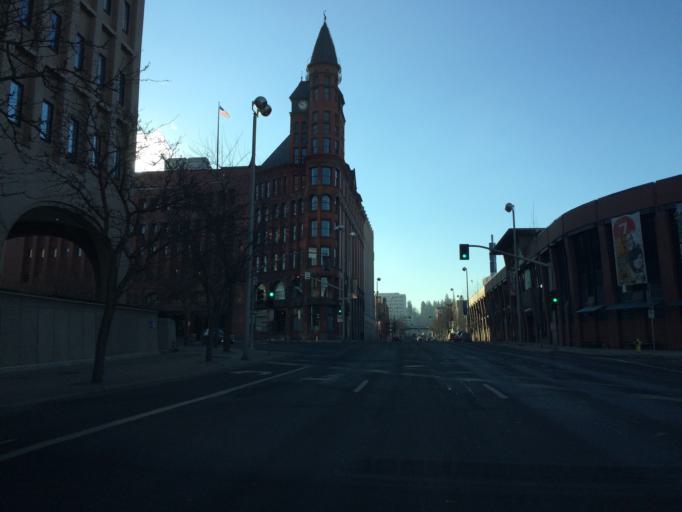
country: US
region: Washington
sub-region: Spokane County
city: Spokane
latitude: 47.6587
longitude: -117.4266
